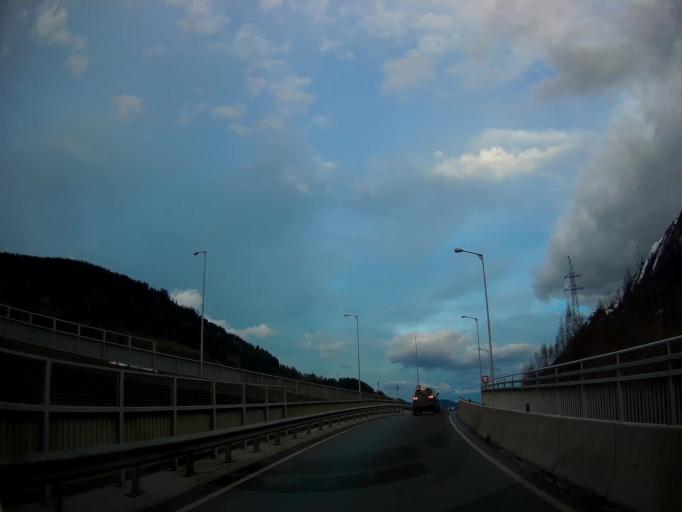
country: AT
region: Salzburg
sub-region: Politischer Bezirk Zell am See
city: Lend
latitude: 47.2941
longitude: 13.0587
